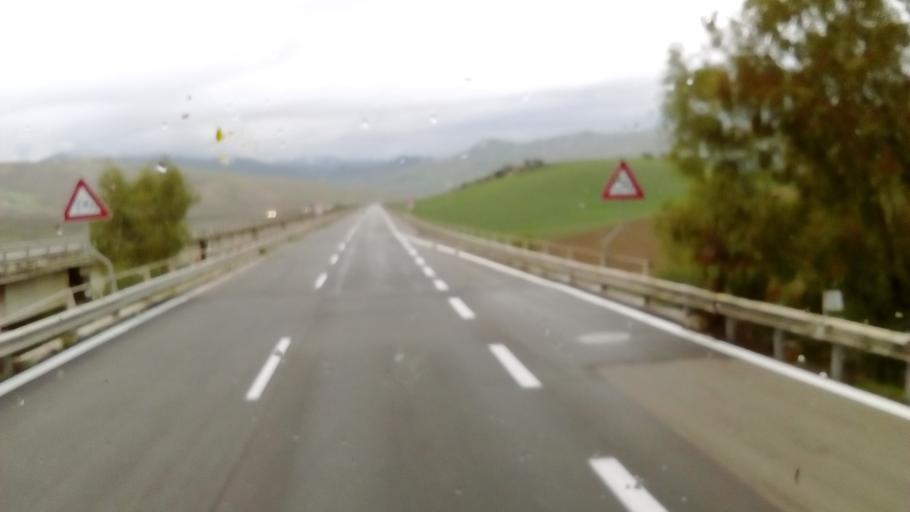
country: IT
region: Sicily
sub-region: Enna
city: Calascibetta
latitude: 37.5675
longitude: 14.2269
